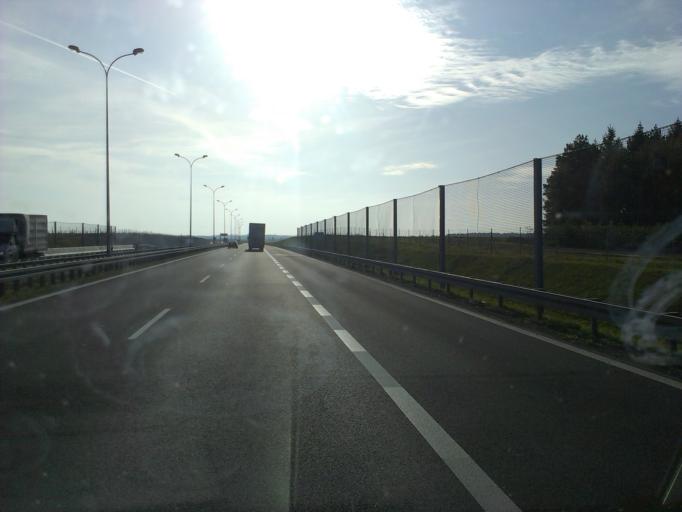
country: PL
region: Lubusz
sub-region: Powiat zielonogorski
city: Sulechow
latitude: 52.1332
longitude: 15.5758
